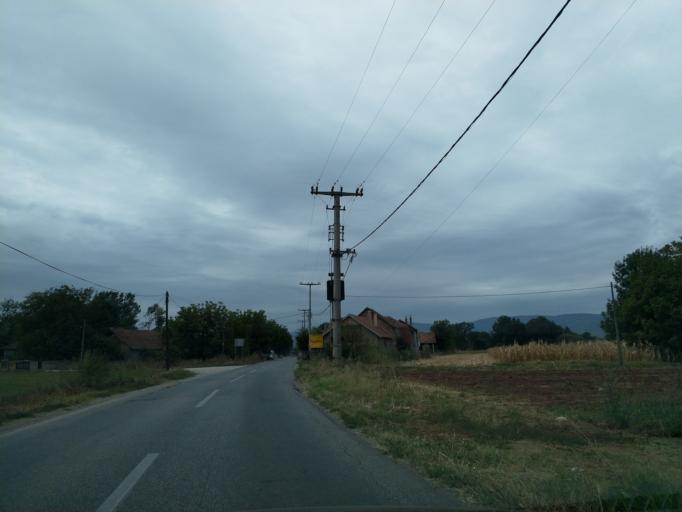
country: RS
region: Central Serbia
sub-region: Pomoravski Okrug
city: Paracin
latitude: 43.8519
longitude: 21.3911
